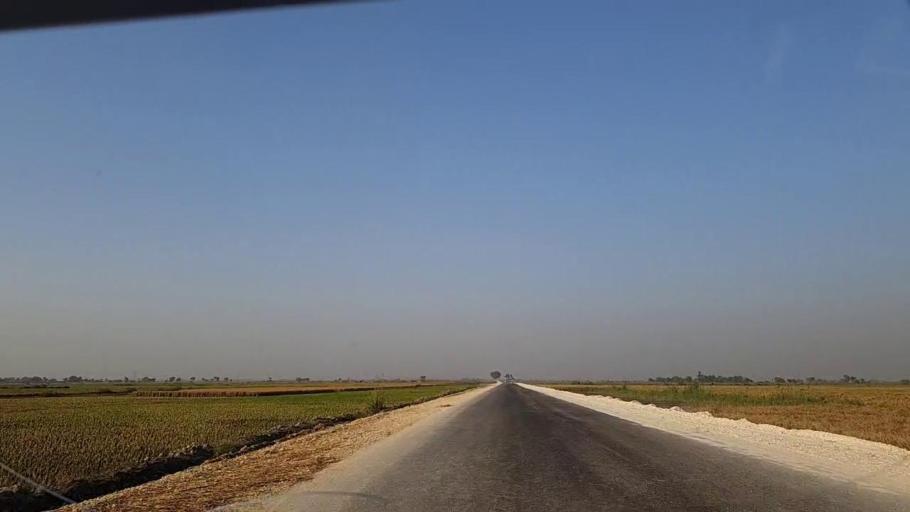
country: PK
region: Sindh
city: Rustam jo Goth
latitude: 27.9808
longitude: 68.8062
